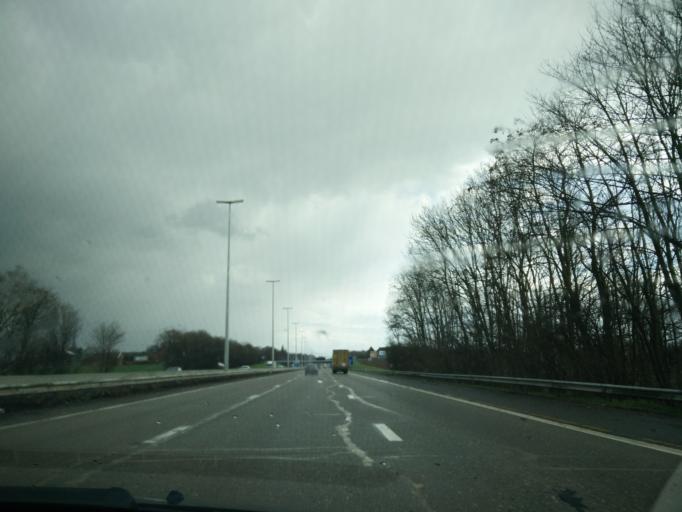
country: BE
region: Wallonia
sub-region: Province de Liege
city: Awans
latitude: 50.6812
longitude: 5.4442
